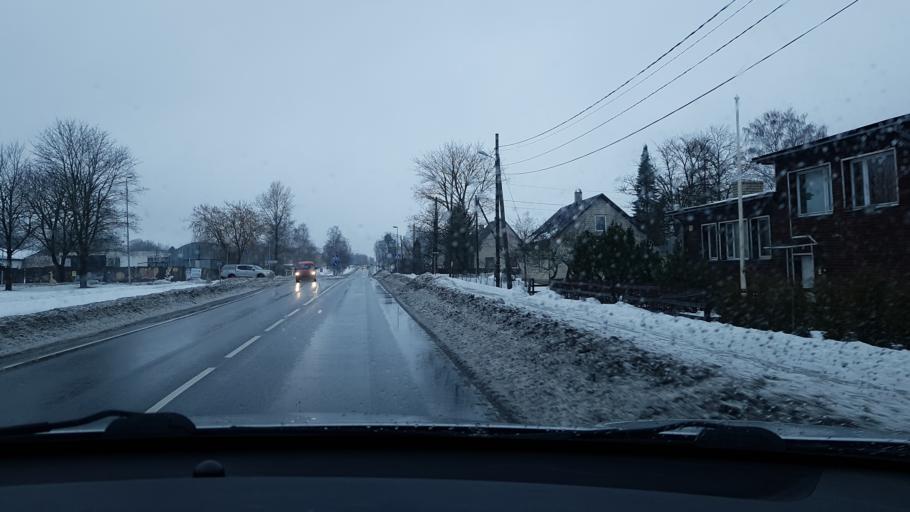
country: EE
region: Jaervamaa
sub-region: Tueri vald
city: Tueri
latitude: 58.8108
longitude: 25.4119
